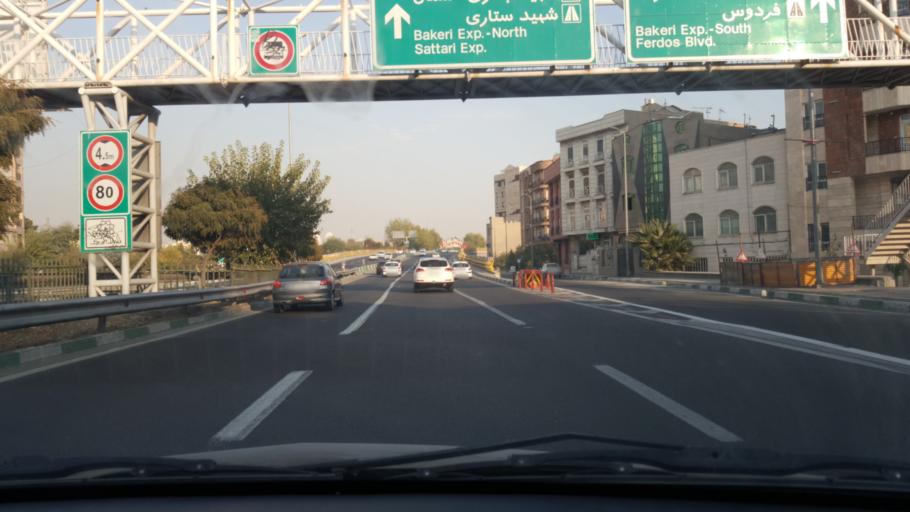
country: IR
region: Tehran
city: Tehran
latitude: 35.7333
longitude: 51.2909
